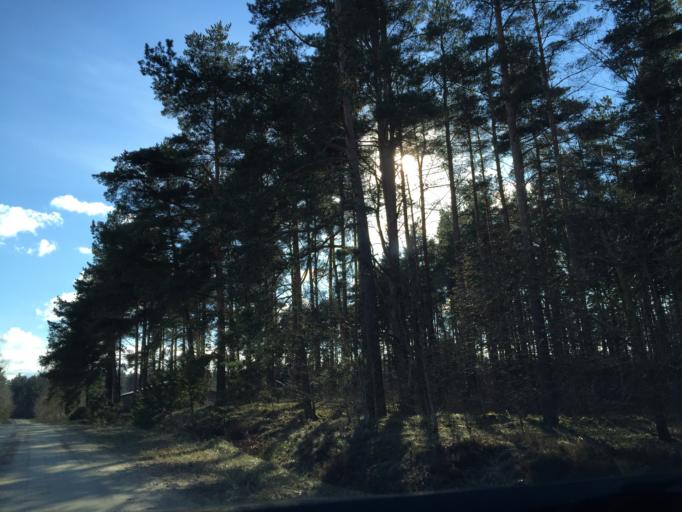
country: LV
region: Kekava
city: Kekava
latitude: 56.8520
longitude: 24.1869
